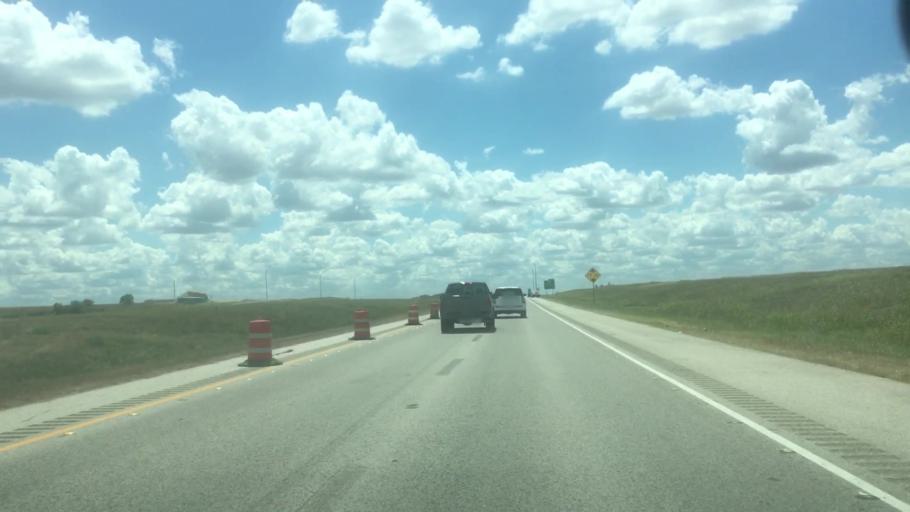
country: US
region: Texas
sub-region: Caldwell County
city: Martindale
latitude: 29.7924
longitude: -97.7834
